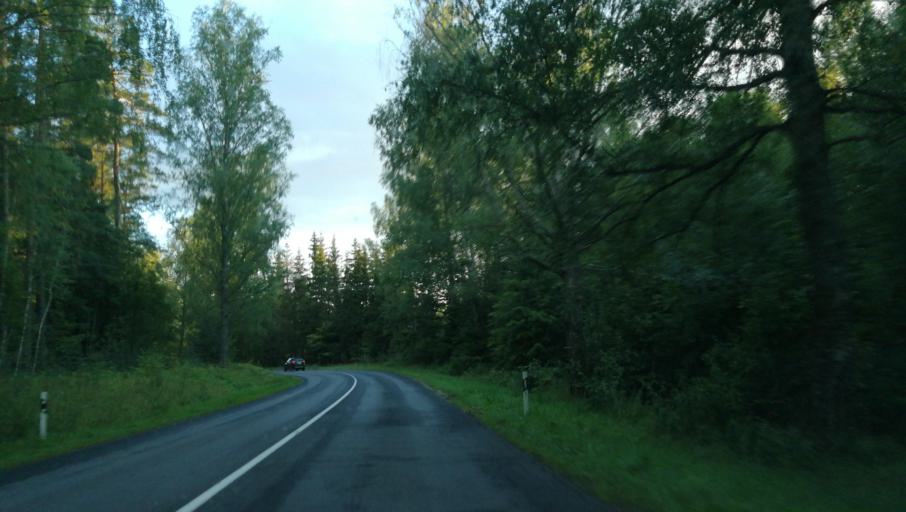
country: LV
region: Priekuli
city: Priekuli
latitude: 57.3682
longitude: 25.3826
